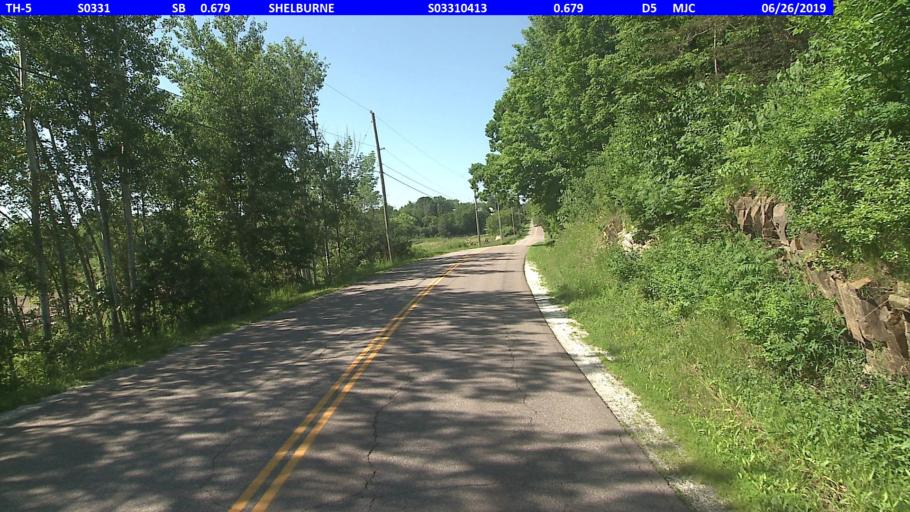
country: US
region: Vermont
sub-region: Chittenden County
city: Hinesburg
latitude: 44.3808
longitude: -73.1775
